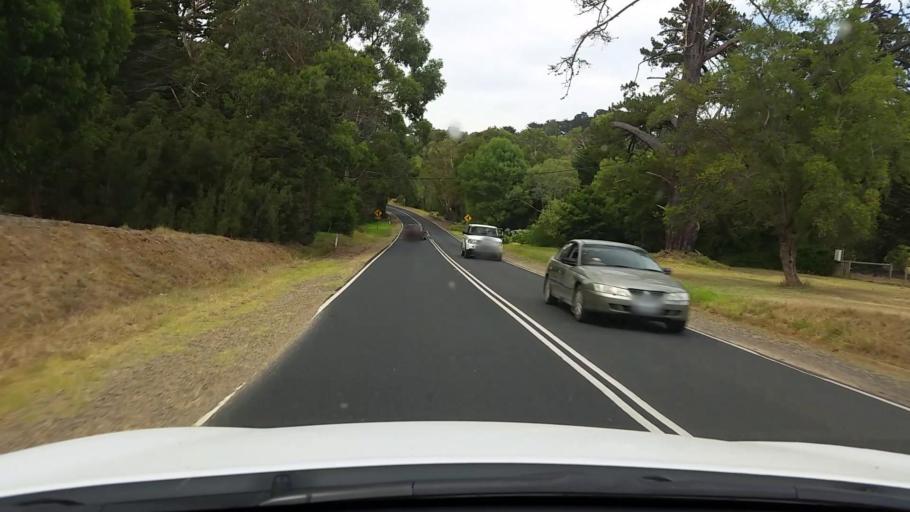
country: AU
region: Victoria
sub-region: Mornington Peninsula
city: Merricks
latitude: -38.4274
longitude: 145.0426
